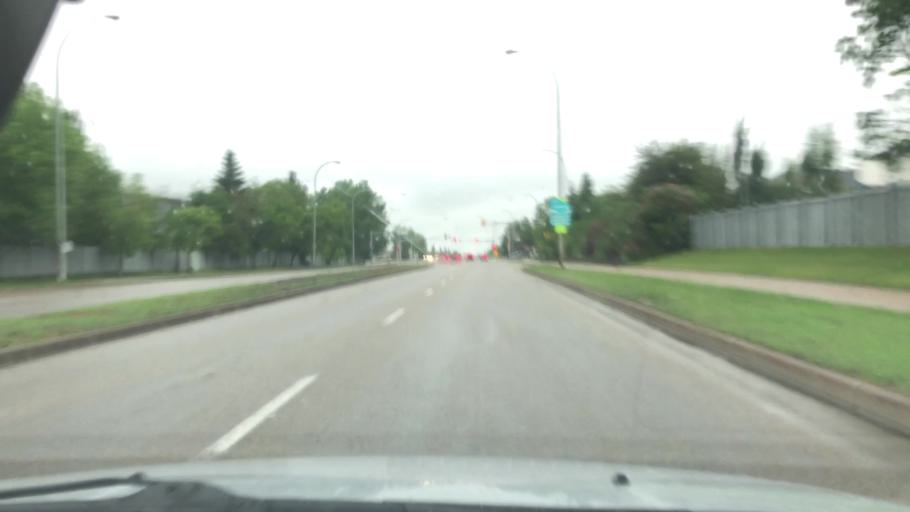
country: CA
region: Alberta
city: Sherwood Park
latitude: 53.5388
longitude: -113.2633
